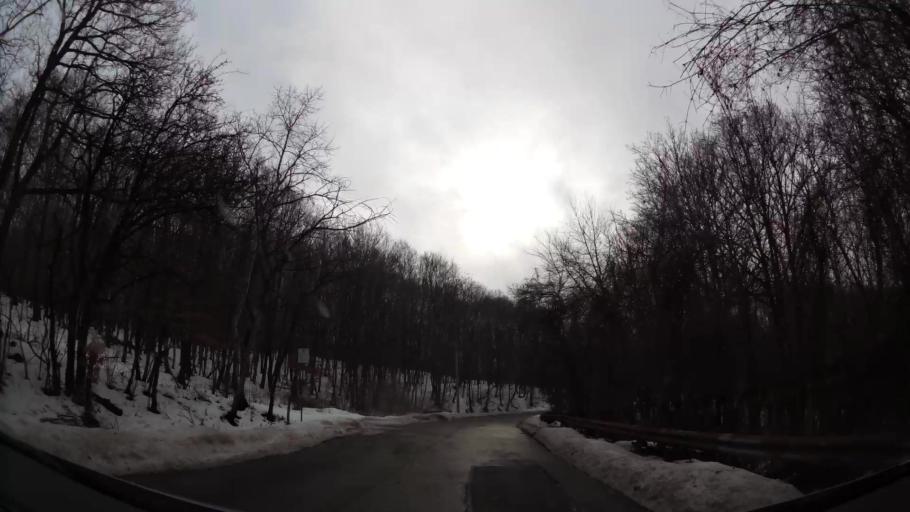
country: BG
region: Sofiya
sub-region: Obshtina Bozhurishte
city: Bozhurishte
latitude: 42.6563
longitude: 23.2024
